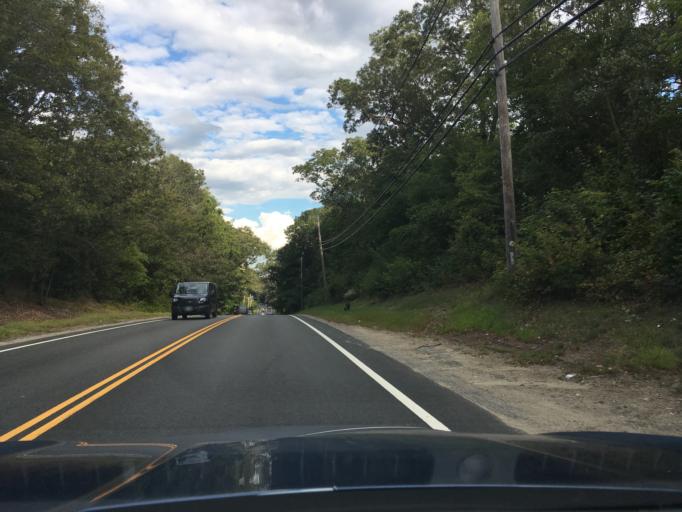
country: US
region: Rhode Island
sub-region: Kent County
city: East Greenwich
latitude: 41.6629
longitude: -71.4858
